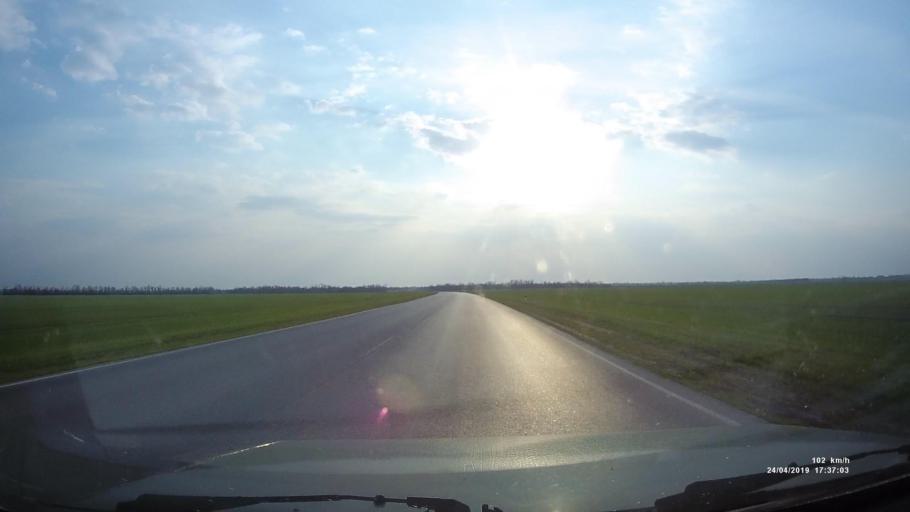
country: RU
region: Rostov
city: Tselina
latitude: 46.5137
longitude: 41.0382
